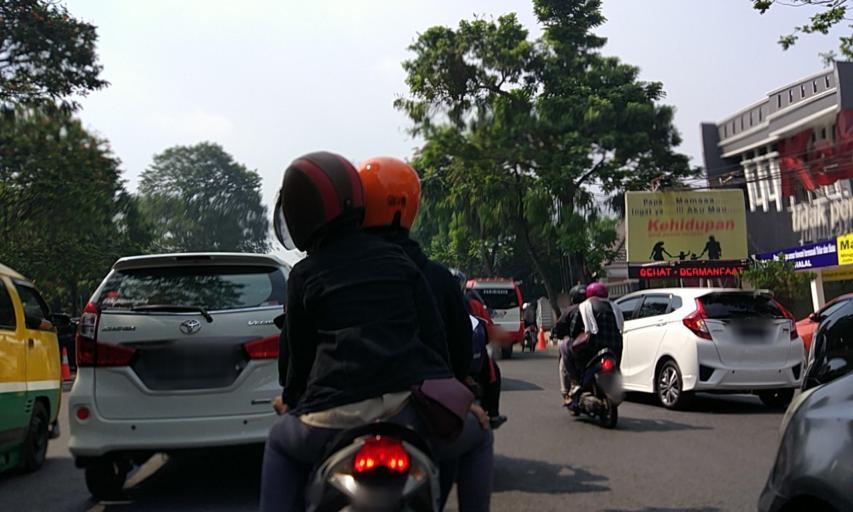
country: ID
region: West Java
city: Bandung
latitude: -6.9066
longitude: 107.5982
